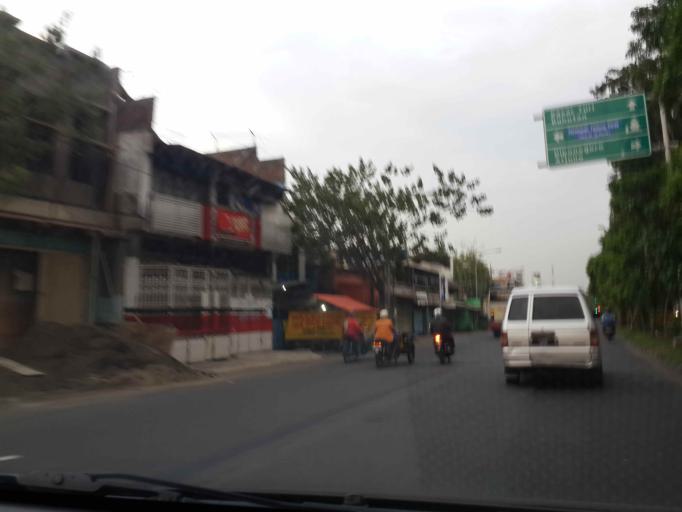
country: ID
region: East Java
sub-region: Kota Surabaya
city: Surabaya
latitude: -7.2451
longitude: 112.7187
